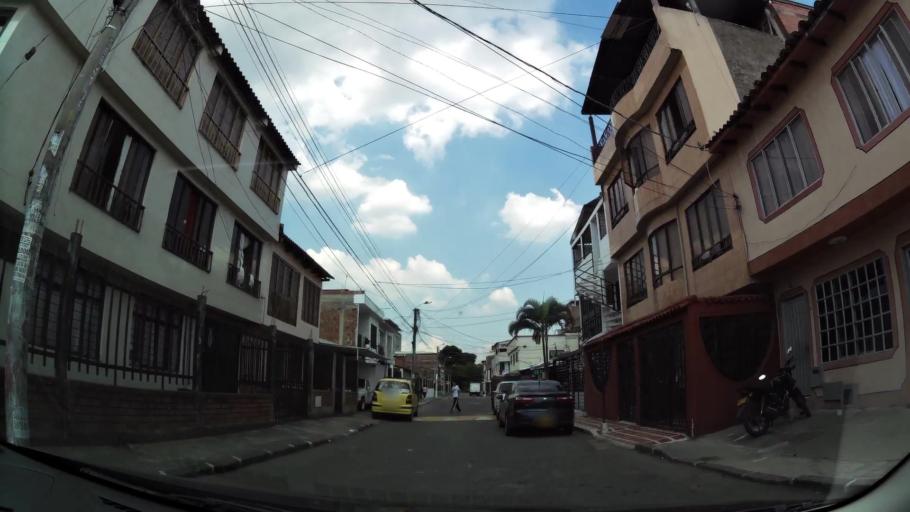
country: CO
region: Valle del Cauca
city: Cali
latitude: 3.4166
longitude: -76.5188
